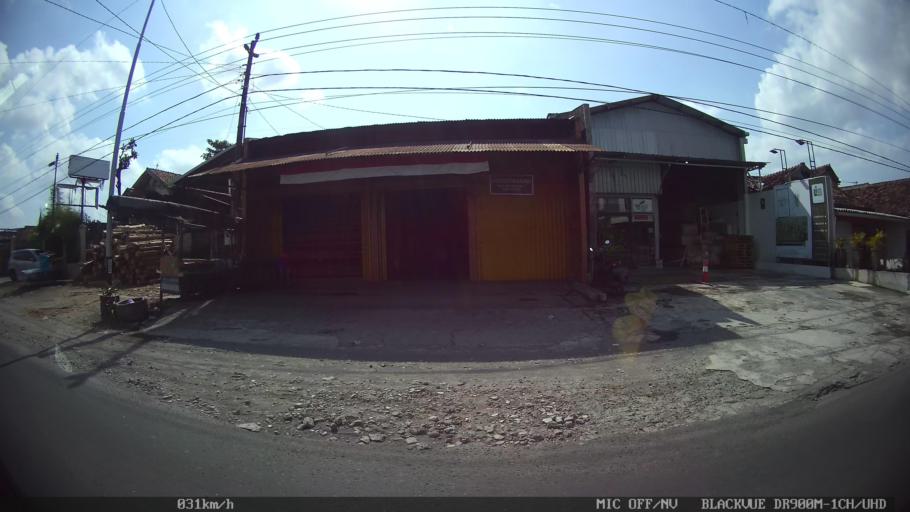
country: ID
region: Daerah Istimewa Yogyakarta
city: Sewon
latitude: -7.8336
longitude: 110.3742
